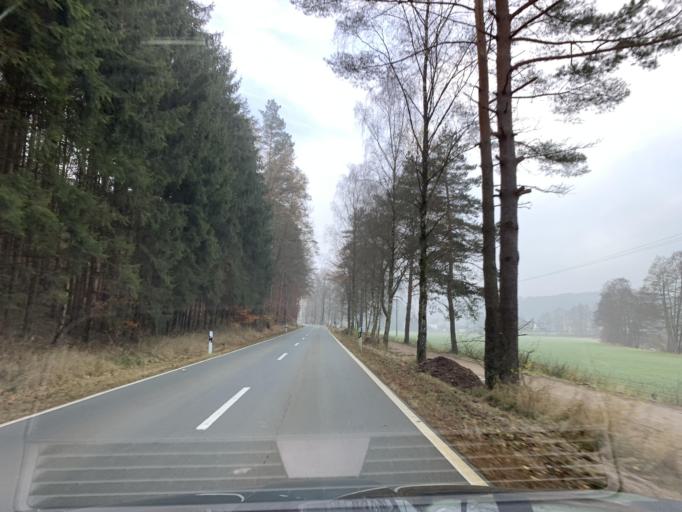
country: DE
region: Bavaria
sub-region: Upper Palatinate
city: Neunburg vorm Wald
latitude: 49.3682
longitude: 12.4033
